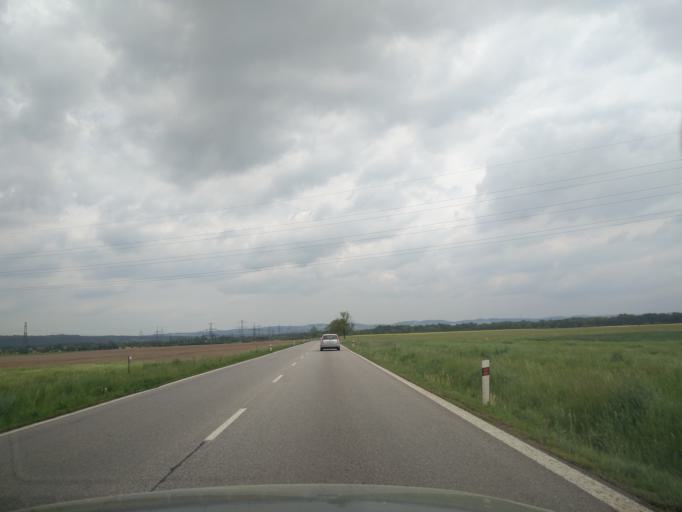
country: CZ
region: Jihocesky
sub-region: Okres Ceske Budejovice
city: Hluboka nad Vltavou
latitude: 49.0184
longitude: 14.4148
